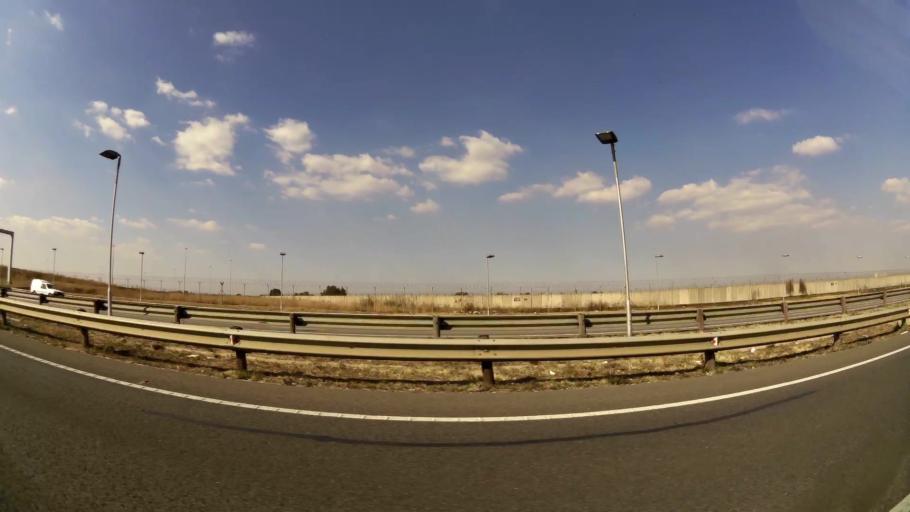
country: ZA
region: Gauteng
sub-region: City of Johannesburg Metropolitan Municipality
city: Modderfontein
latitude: -26.1030
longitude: 28.2488
